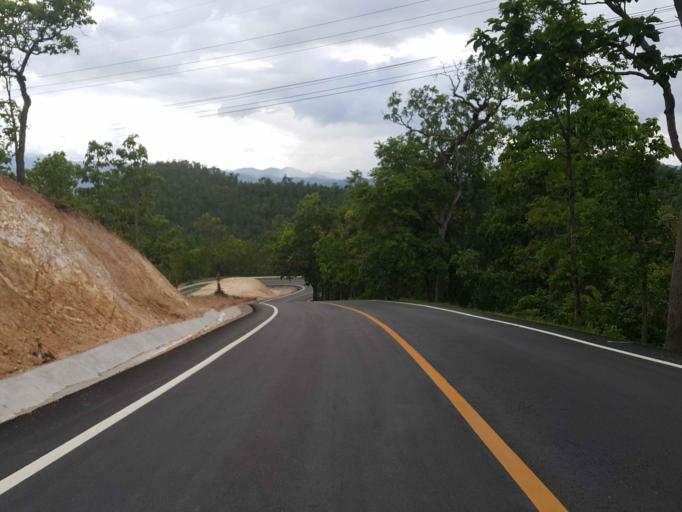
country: TH
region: Chiang Mai
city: Mae Chaem
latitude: 18.5080
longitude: 98.4113
